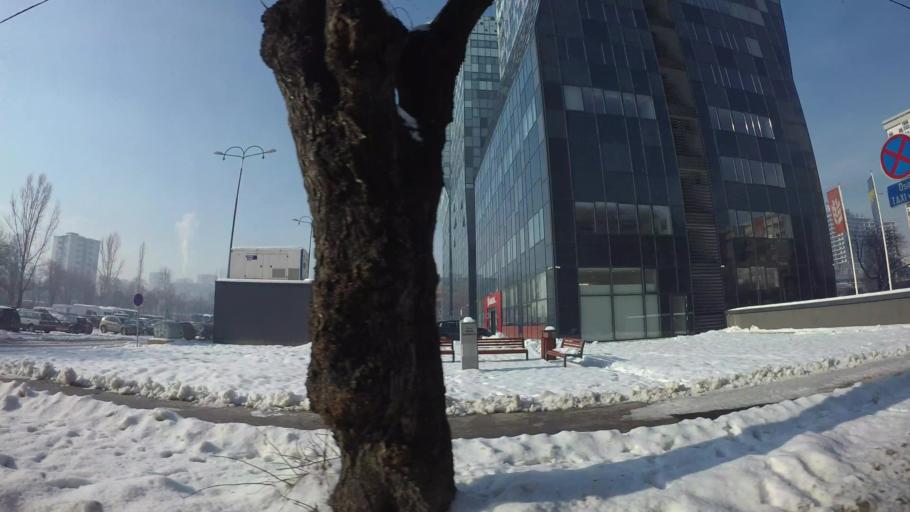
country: BA
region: Federation of Bosnia and Herzegovina
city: Kobilja Glava
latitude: 43.8528
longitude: 18.3895
